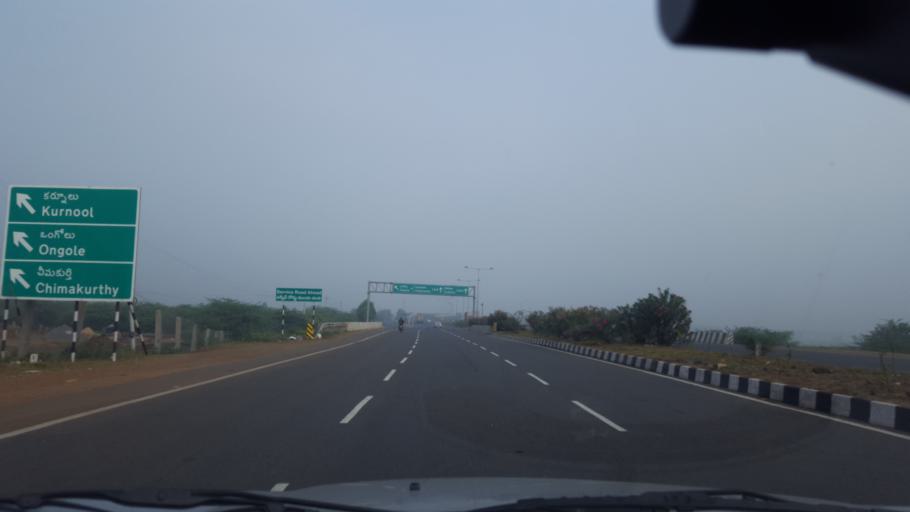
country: IN
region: Andhra Pradesh
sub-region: Prakasam
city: Ongole
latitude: 15.4646
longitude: 80.0479
